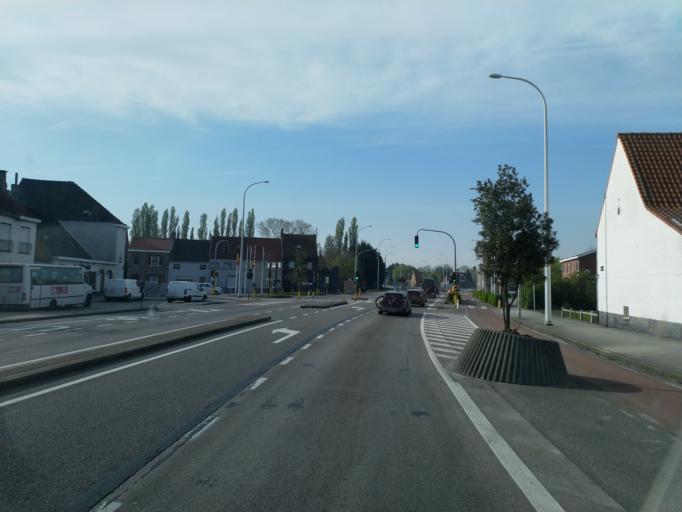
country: BE
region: Flanders
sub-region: Provincie West-Vlaanderen
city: Zeebrugge
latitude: 51.2946
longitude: 3.1922
